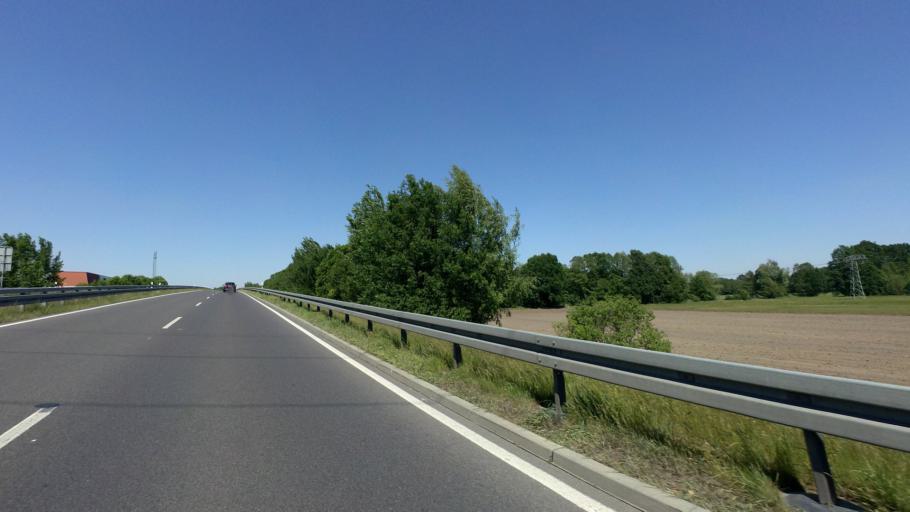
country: DE
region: Brandenburg
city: Peitz
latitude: 51.8144
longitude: 14.3896
